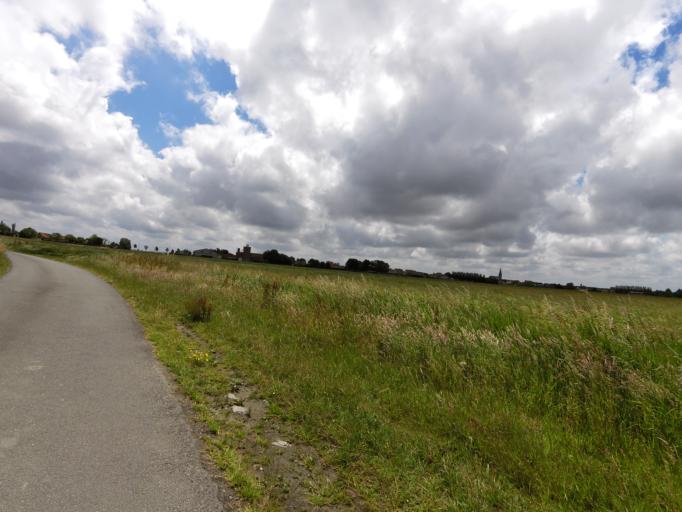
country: BE
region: Flanders
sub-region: Provincie West-Vlaanderen
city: Gistel
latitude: 51.1428
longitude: 2.9267
